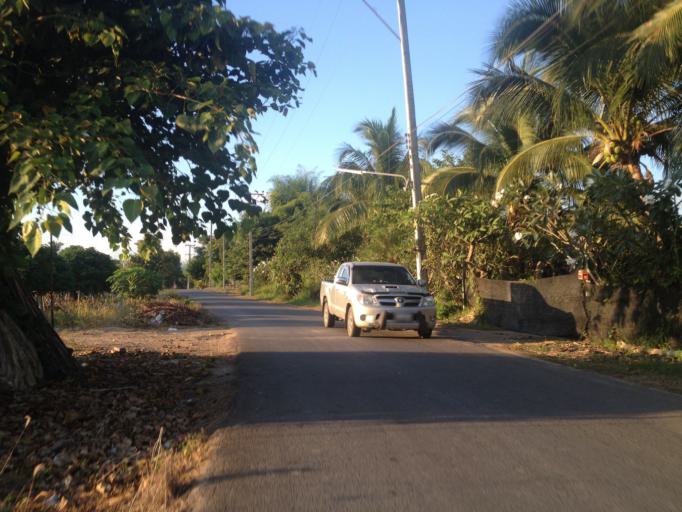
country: TH
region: Chiang Mai
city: Hang Dong
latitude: 18.6669
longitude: 98.8850
